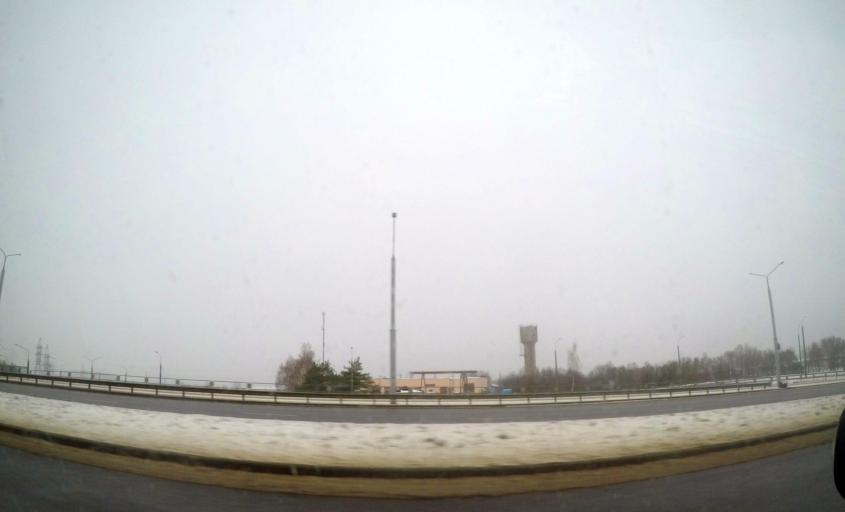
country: BY
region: Grodnenskaya
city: Hrodna
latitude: 53.6357
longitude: 23.8105
